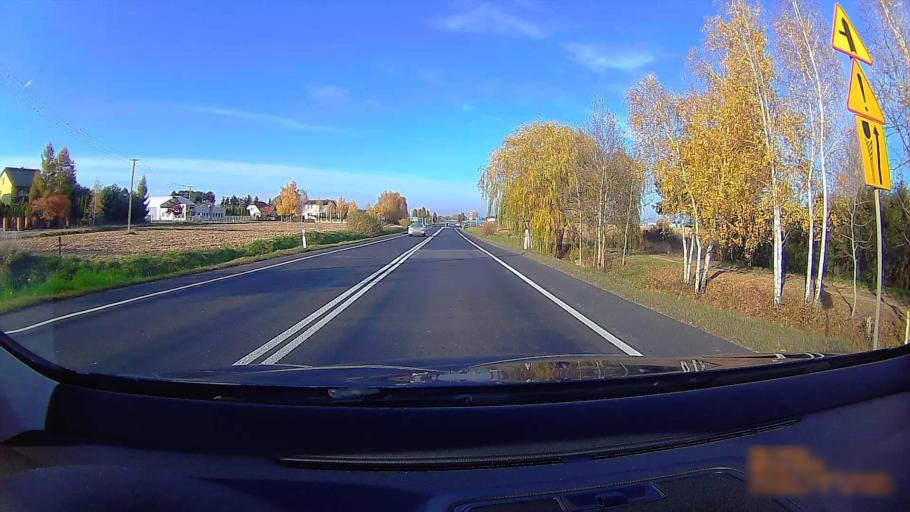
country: PL
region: Greater Poland Voivodeship
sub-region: Powiat koninski
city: Stare Miasto
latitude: 52.1560
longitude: 18.2056
